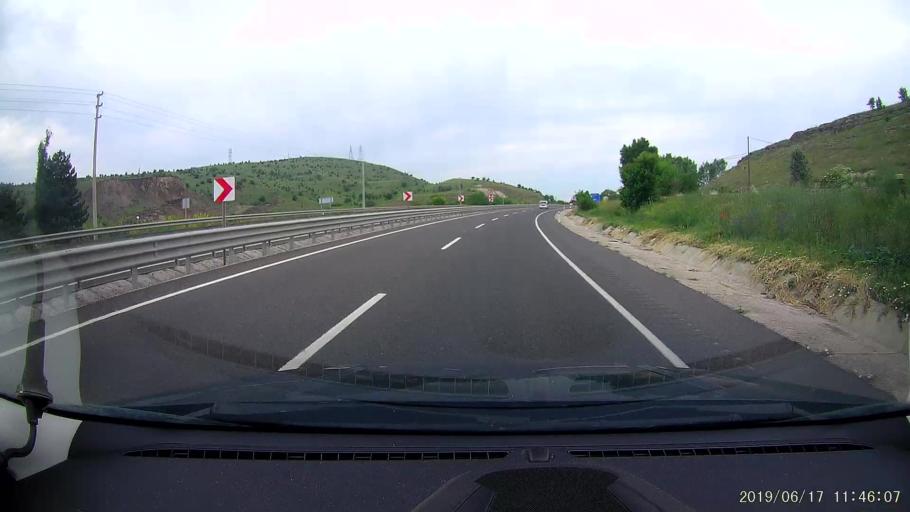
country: TR
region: Cankiri
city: Kursunlu
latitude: 40.8476
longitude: 33.2375
